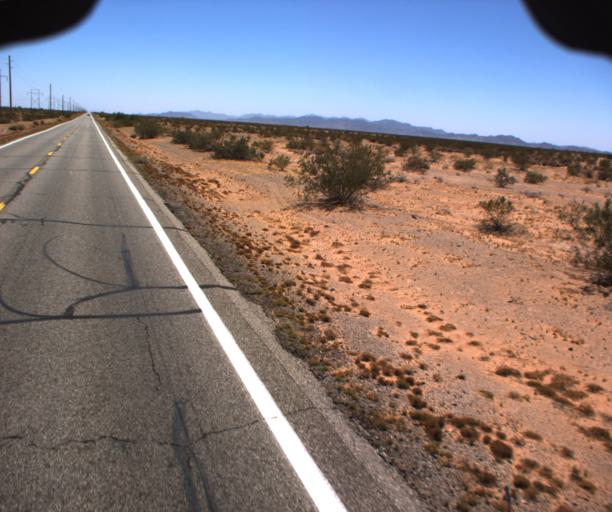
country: US
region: Arizona
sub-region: La Paz County
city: Quartzsite
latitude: 33.8742
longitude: -114.2170
